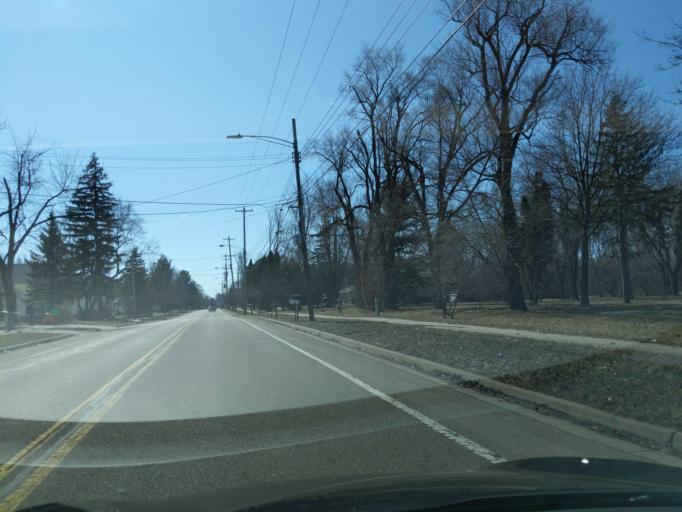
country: US
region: Michigan
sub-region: Ingham County
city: Holt
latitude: 42.6598
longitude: -84.5643
